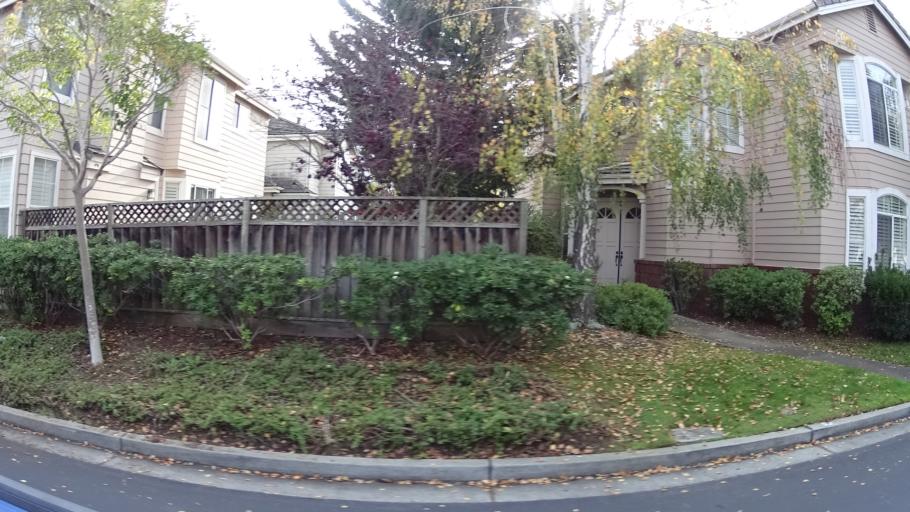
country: US
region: California
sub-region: San Mateo County
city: Redwood Shores
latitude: 37.5400
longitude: -122.2333
